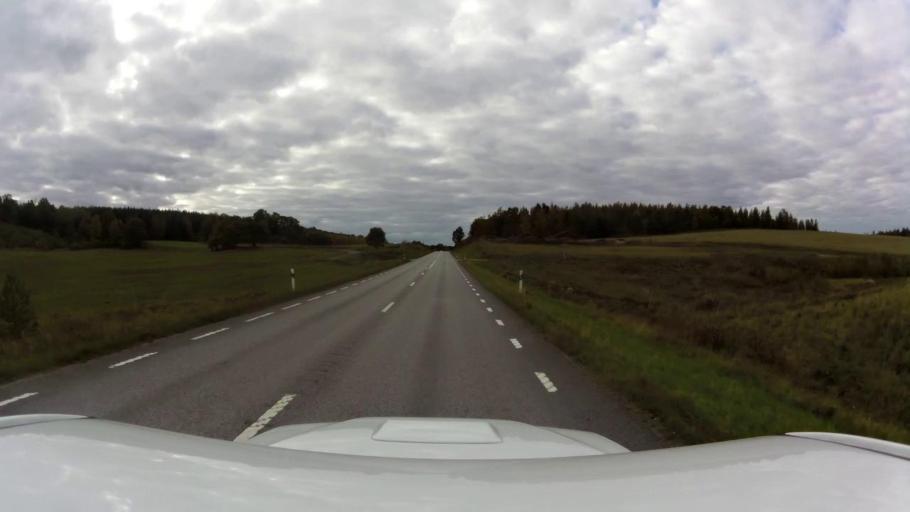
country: SE
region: OEstergoetland
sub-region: Kinda Kommun
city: Rimforsa
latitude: 58.1971
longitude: 15.6675
